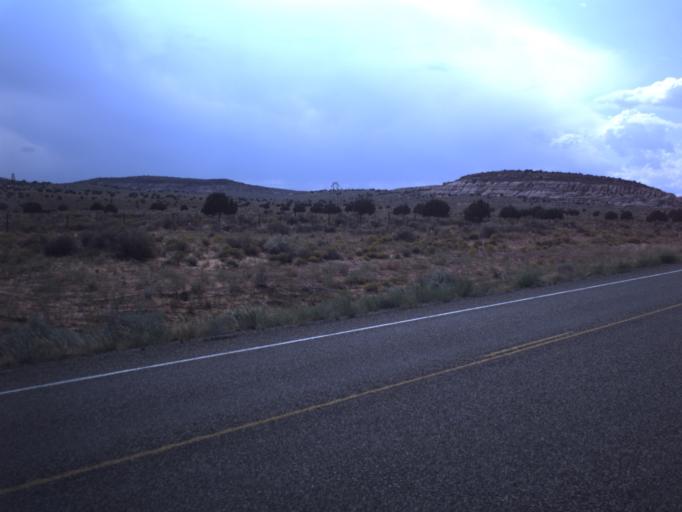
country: US
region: Arizona
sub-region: Coconino County
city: Page
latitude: 37.0854
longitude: -111.6834
